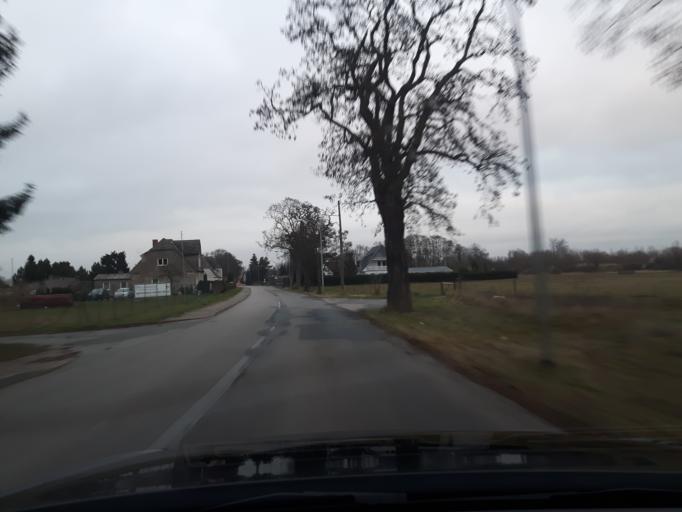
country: DE
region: Mecklenburg-Vorpommern
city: Tribsees
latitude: 54.0763
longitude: 12.7210
